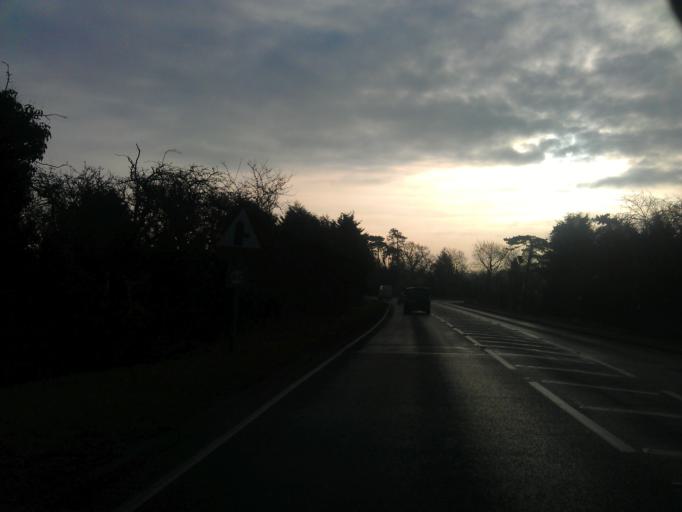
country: GB
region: England
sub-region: Essex
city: Alresford
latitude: 51.8533
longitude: 1.0070
